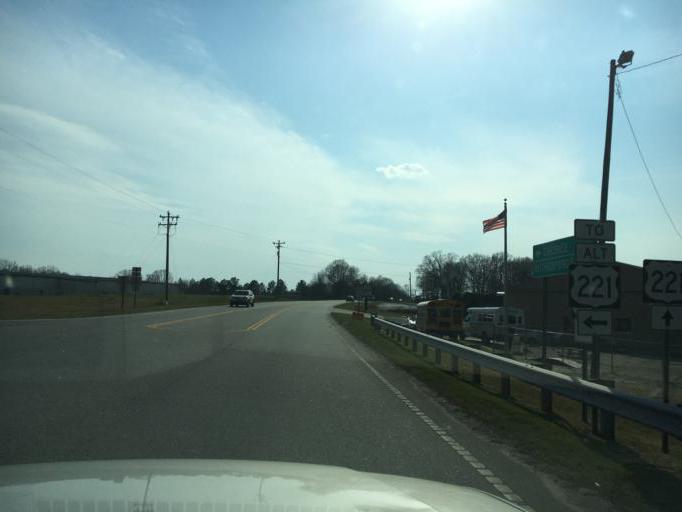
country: US
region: South Carolina
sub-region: Spartanburg County
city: Mayo
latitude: 35.1546
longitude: -81.8519
